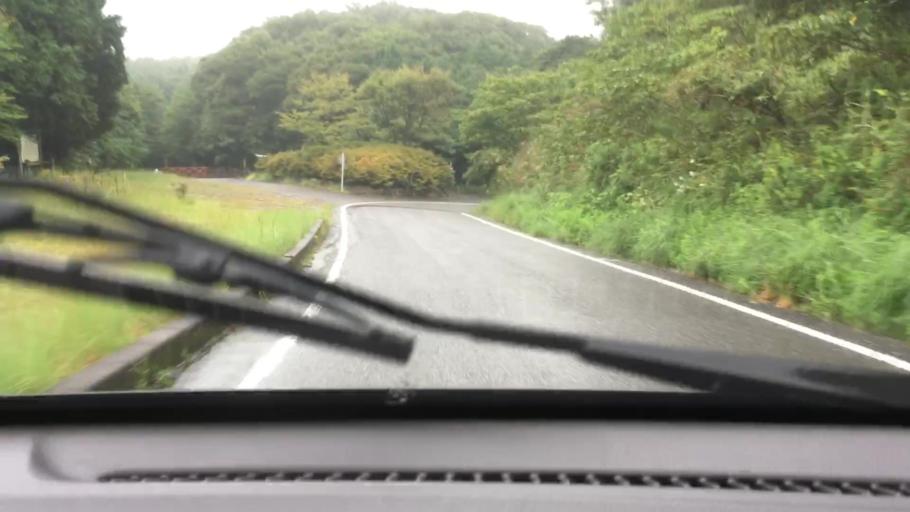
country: JP
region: Nagasaki
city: Togitsu
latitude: 32.9169
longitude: 129.7268
